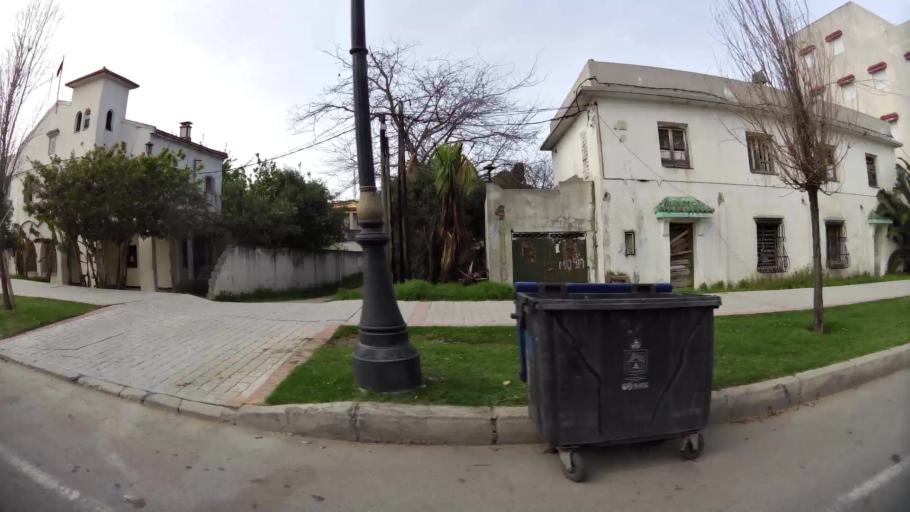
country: MA
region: Tanger-Tetouan
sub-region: Tanger-Assilah
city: Tangier
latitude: 35.7581
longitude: -5.8452
